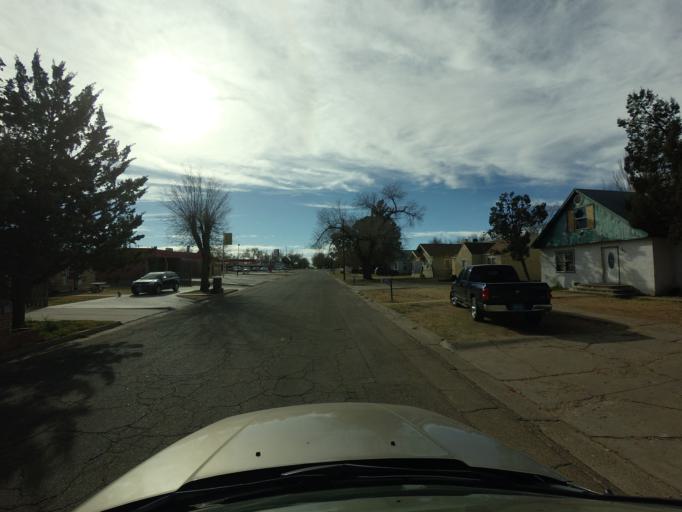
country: US
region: New Mexico
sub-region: Curry County
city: Clovis
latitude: 34.4156
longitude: -103.2029
